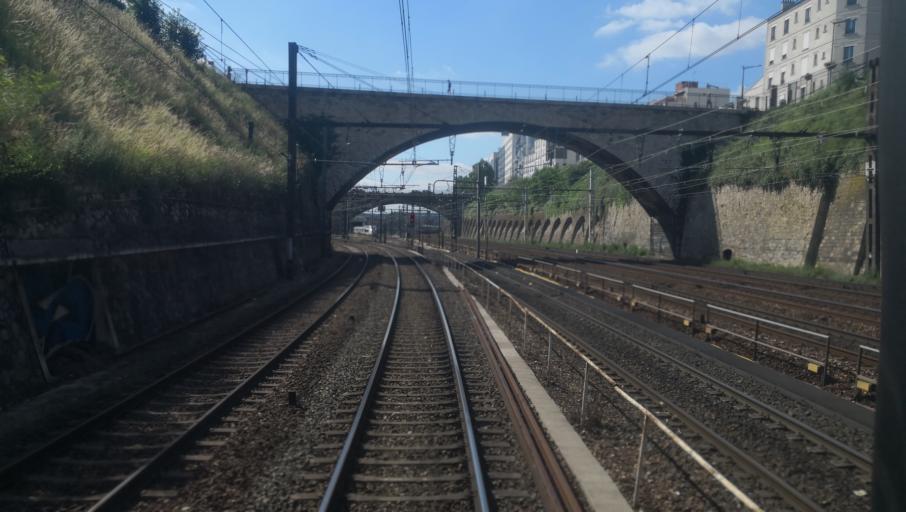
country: FR
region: Ile-de-France
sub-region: Departement du Val-de-Marne
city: Charenton-le-Pont
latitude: 48.8234
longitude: 2.4077
